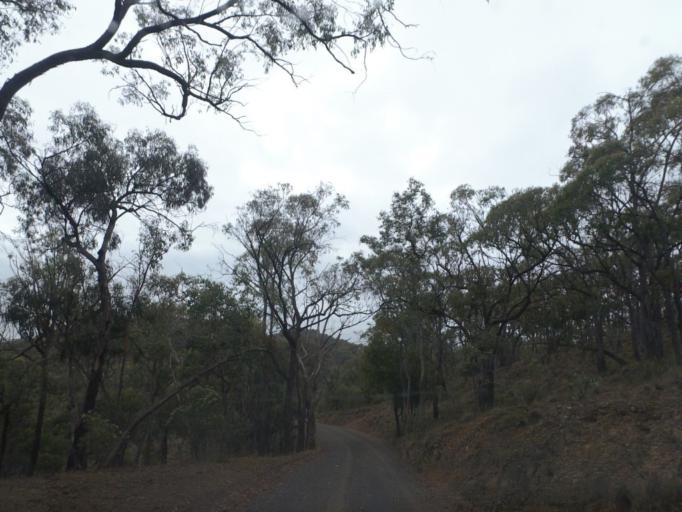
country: AU
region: Victoria
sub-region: Nillumbik
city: Saint Andrews
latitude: -37.6071
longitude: 145.2916
